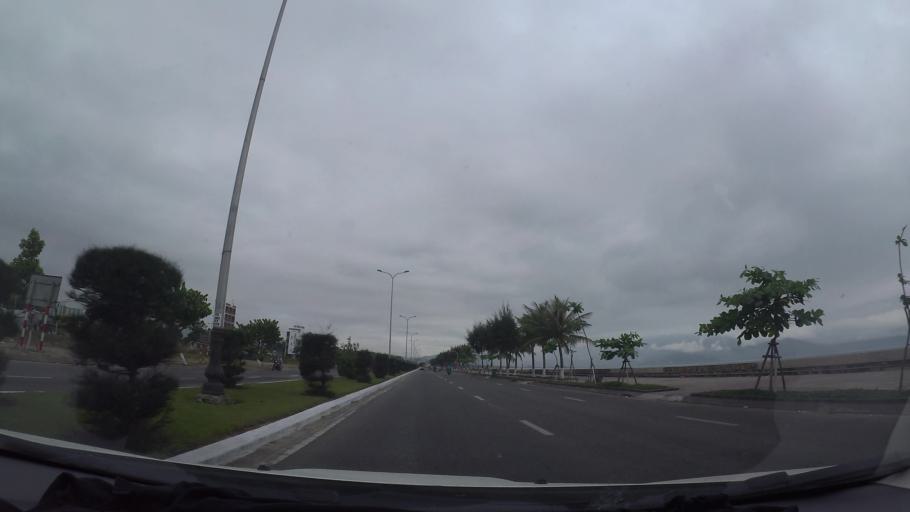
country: VN
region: Da Nang
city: Lien Chieu
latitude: 16.0821
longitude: 108.1654
